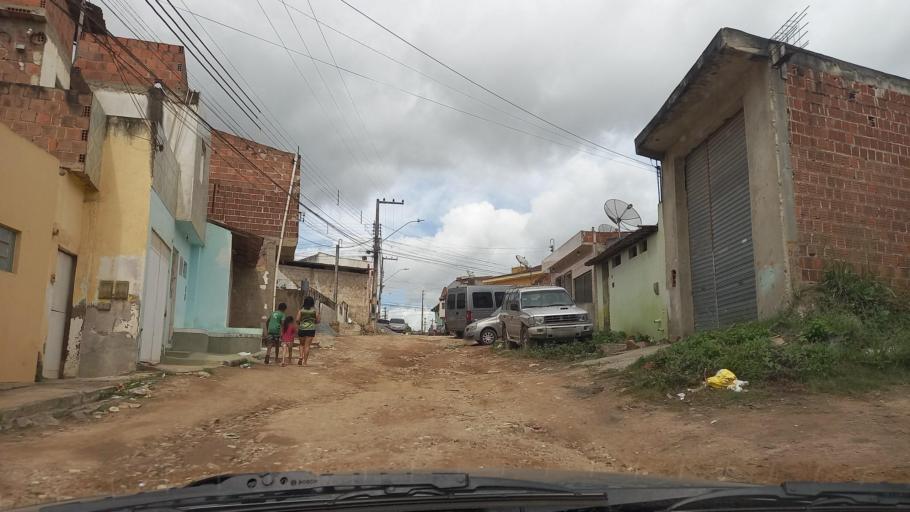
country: ET
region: Oromiya
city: Gore
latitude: 8.1959
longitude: 35.5782
